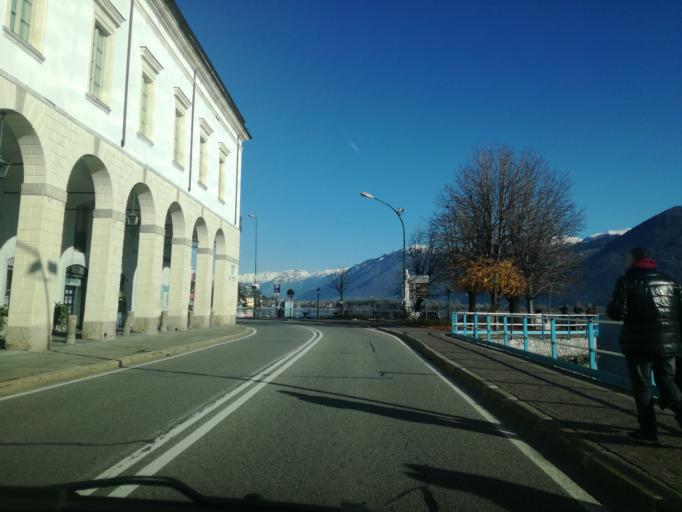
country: IT
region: Lombardy
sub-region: Provincia di Bergamo
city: Lovere
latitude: 45.8146
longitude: 10.0731
